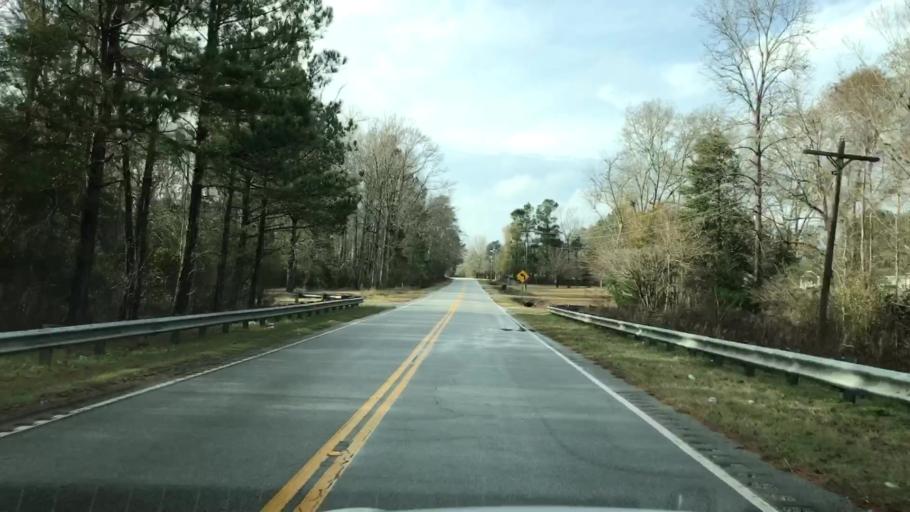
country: US
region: South Carolina
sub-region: Williamsburg County
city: Andrews
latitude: 33.4998
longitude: -79.5143
